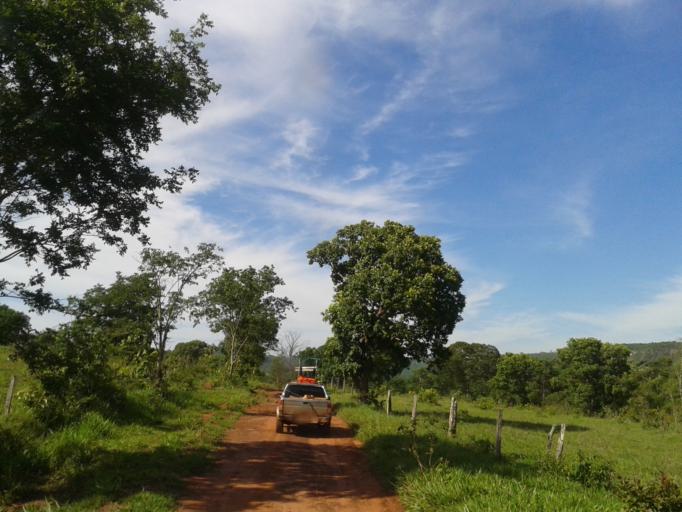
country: BR
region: Minas Gerais
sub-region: Santa Vitoria
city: Santa Vitoria
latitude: -19.0785
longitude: -50.0151
